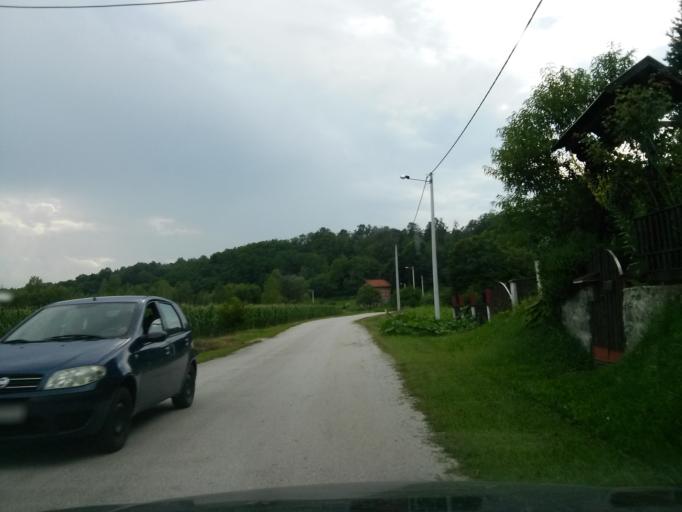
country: HR
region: Sisacko-Moslavacka
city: Glina
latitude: 45.3079
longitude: 15.9914
